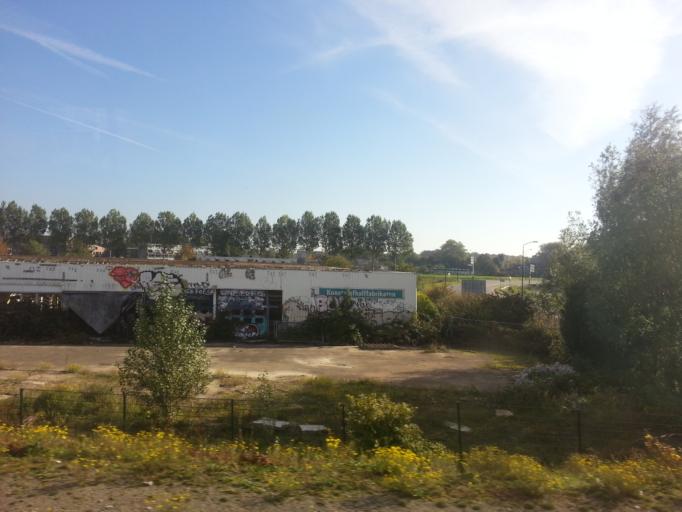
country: NL
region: Utrecht
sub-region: Stichtse Vecht
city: Breukelen
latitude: 52.1723
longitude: 4.9913
